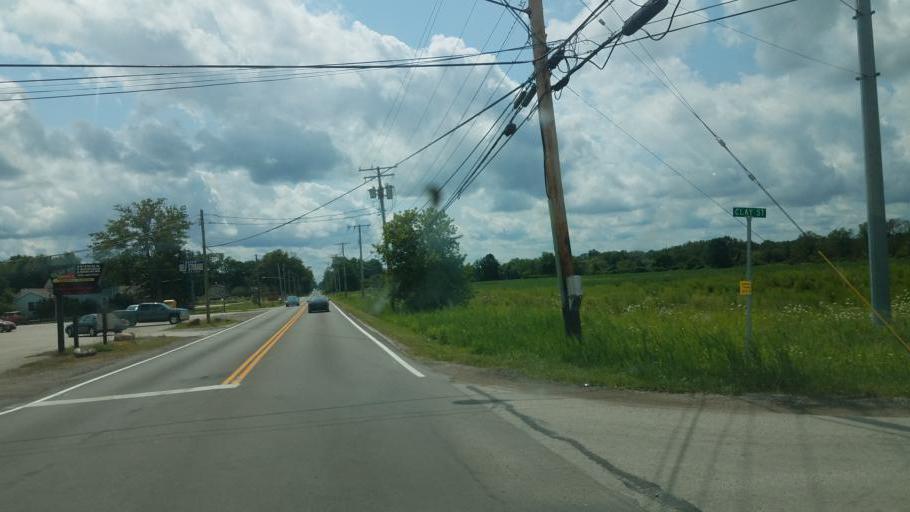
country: US
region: Ohio
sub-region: Ashtabula County
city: Jefferson
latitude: 41.7821
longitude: -80.8550
